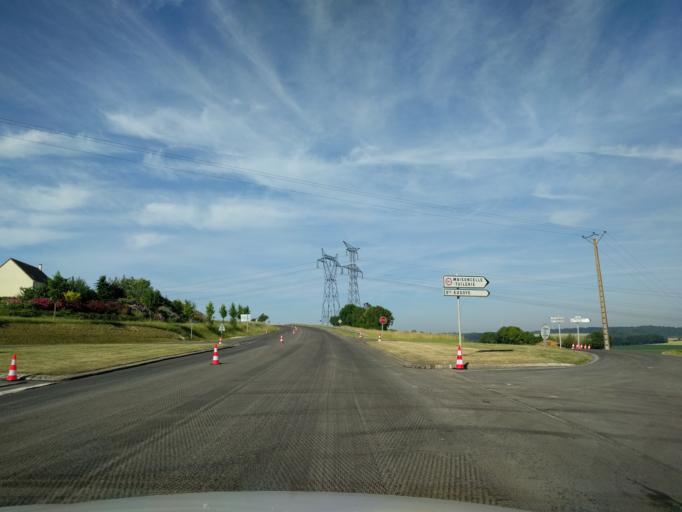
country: FR
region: Picardie
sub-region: Departement de l'Oise
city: Breteuil
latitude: 49.5787
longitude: 2.2392
